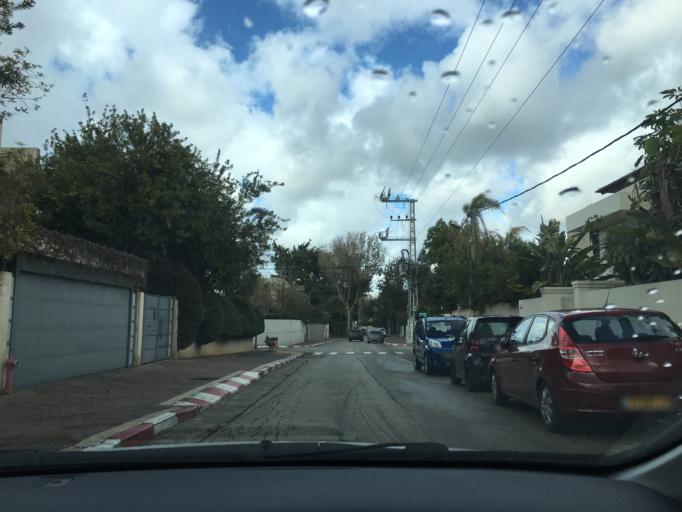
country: IL
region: Tel Aviv
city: Ramat HaSharon
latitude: 32.1486
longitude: 34.8338
